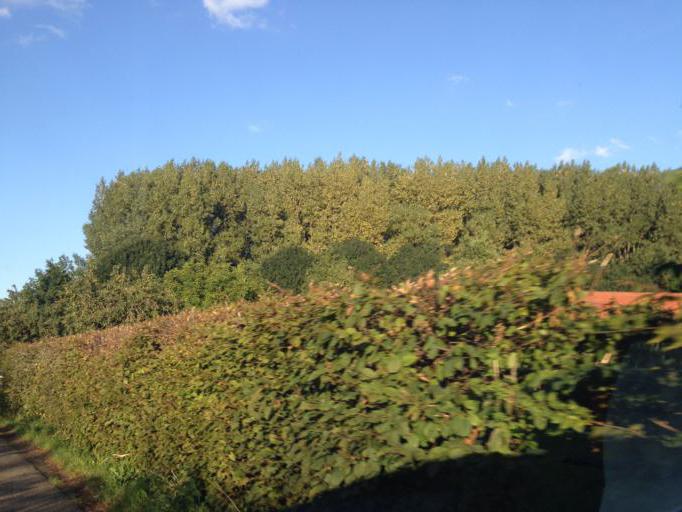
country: NL
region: South Holland
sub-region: Gemeente Leerdam
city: Leerdam
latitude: 51.8715
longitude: 5.1362
